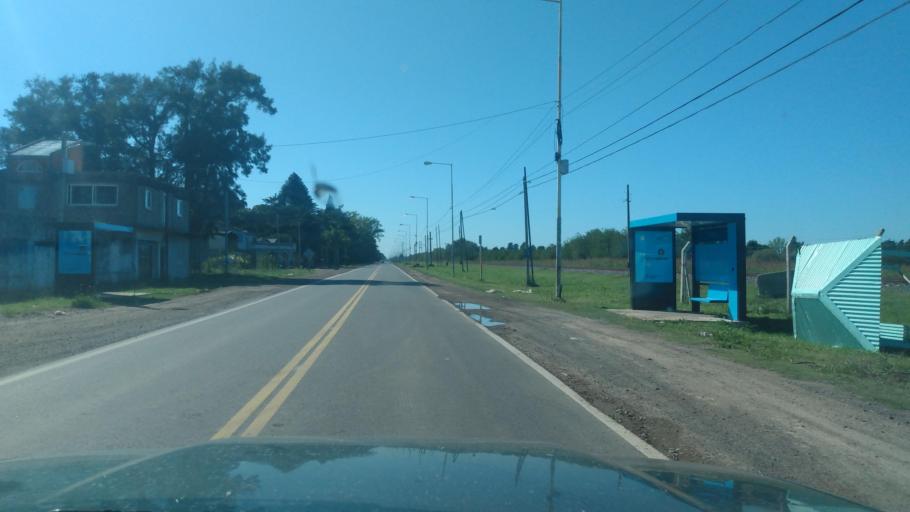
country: AR
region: Buenos Aires
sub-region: Partido de General Rodriguez
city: General Rodriguez
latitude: -34.5922
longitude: -59.0236
